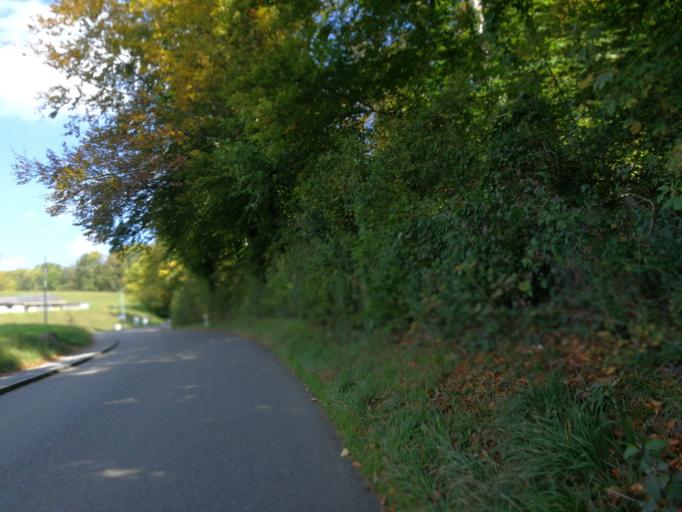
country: CH
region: Zurich
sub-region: Bezirk Meilen
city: Obermeilen
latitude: 47.2796
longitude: 8.6637
